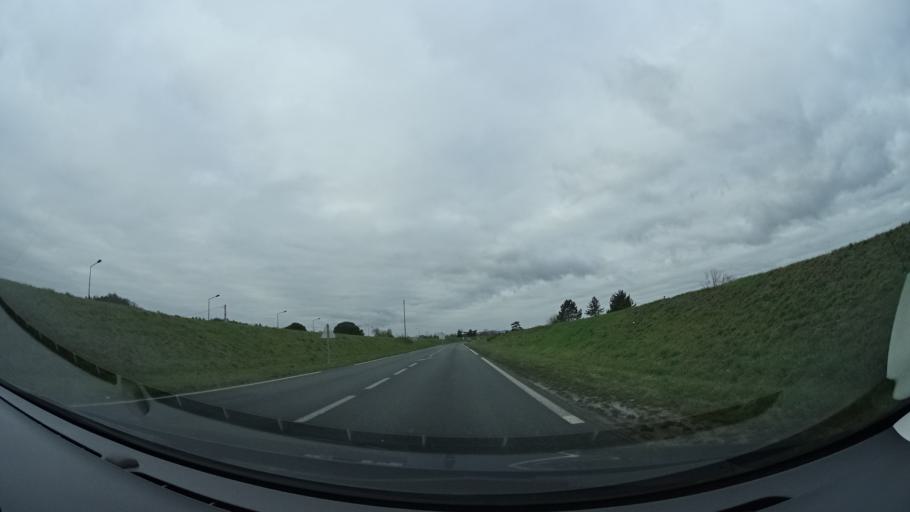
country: FR
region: Aquitaine
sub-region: Departement du Lot-et-Garonne
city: Pujols
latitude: 44.3949
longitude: 0.6921
